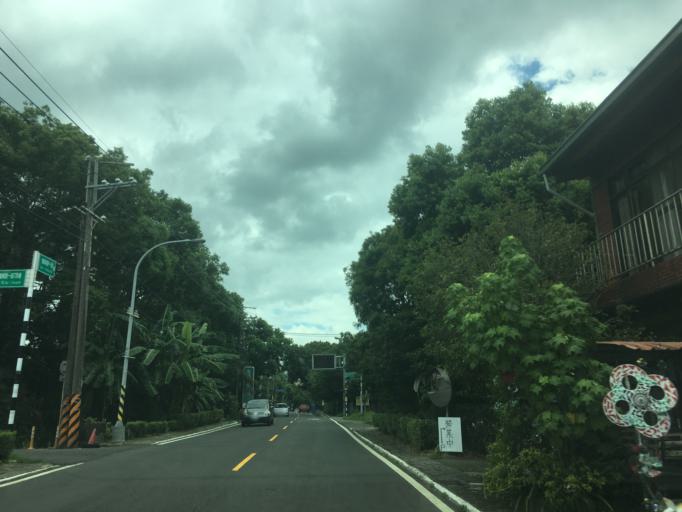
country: TW
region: Taiwan
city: Daxi
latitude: 24.8515
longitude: 121.2889
